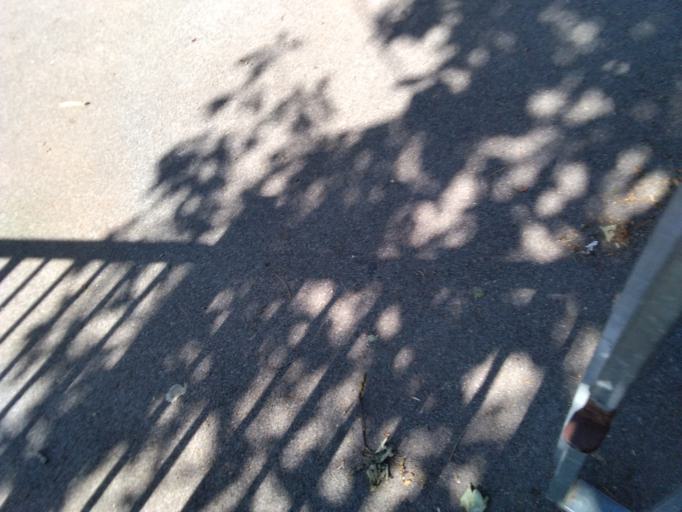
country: FR
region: Picardie
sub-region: Departement de la Somme
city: Rivery
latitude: 49.9109
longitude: 2.3239
